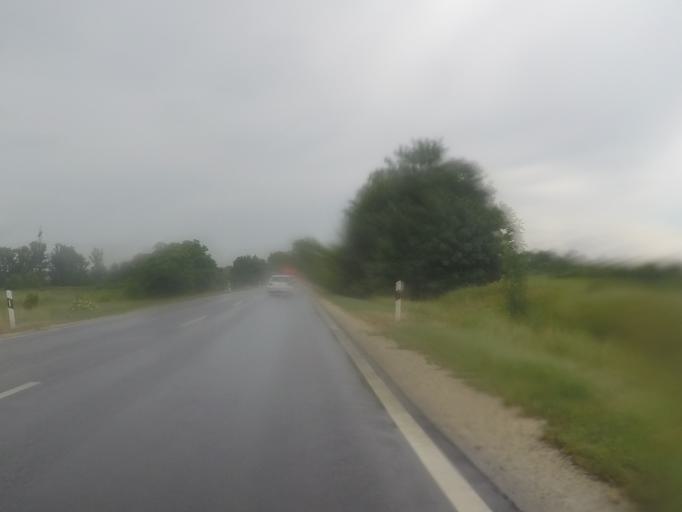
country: HU
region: Veszprem
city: Veszprem
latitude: 47.1338
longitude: 17.9477
